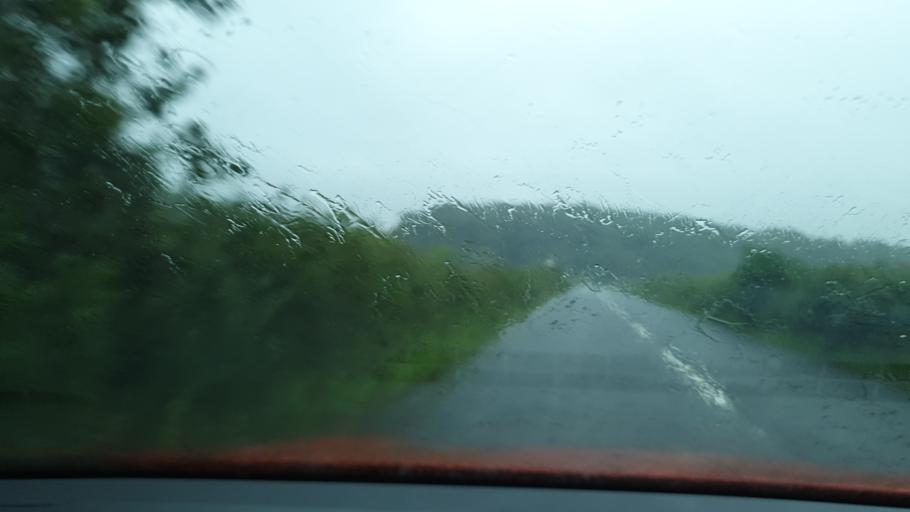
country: GB
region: England
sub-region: Cumbria
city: Millom
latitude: 54.2700
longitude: -3.2195
